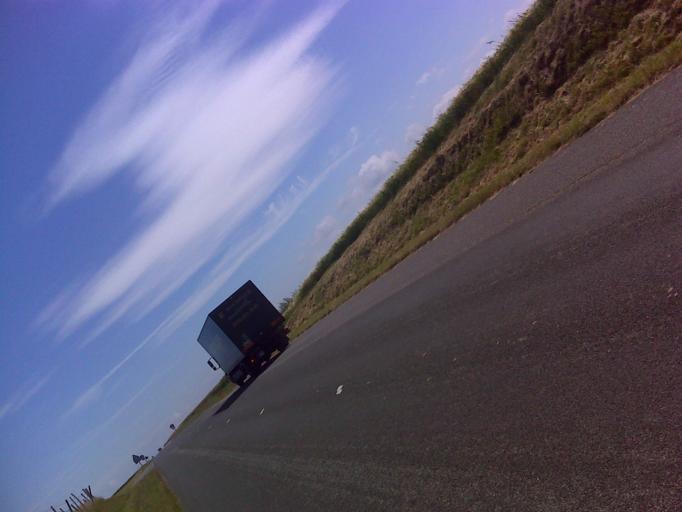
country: FR
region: Haute-Normandie
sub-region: Departement de la Seine-Maritime
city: Le Treport
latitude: 50.0492
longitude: 1.3386
